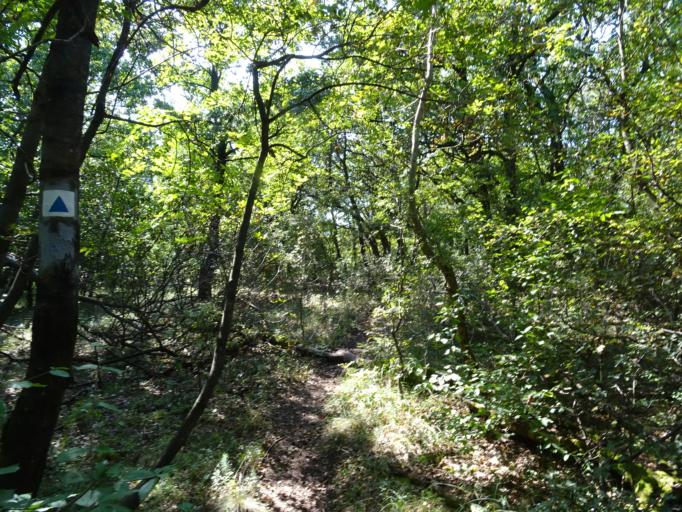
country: HU
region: Fejer
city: Zamoly
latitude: 47.3784
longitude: 18.3836
